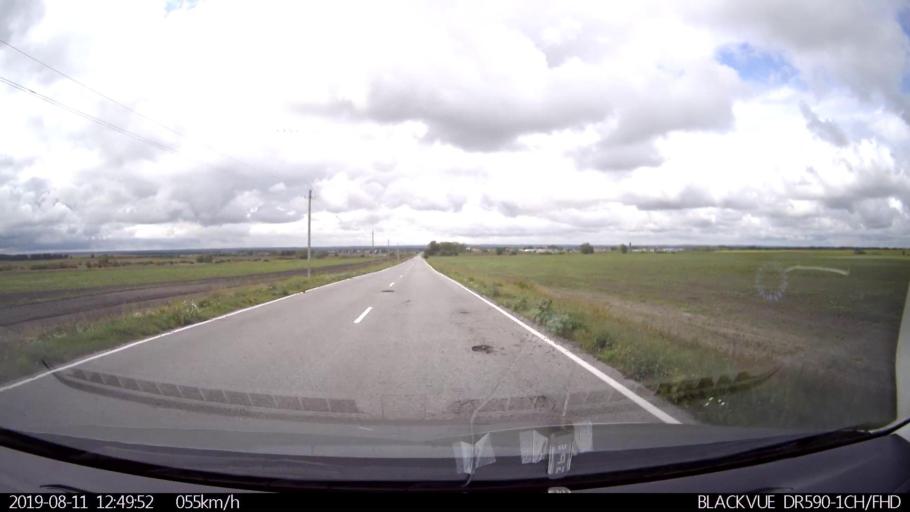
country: RU
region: Ulyanovsk
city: Ignatovka
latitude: 53.8758
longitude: 47.6805
